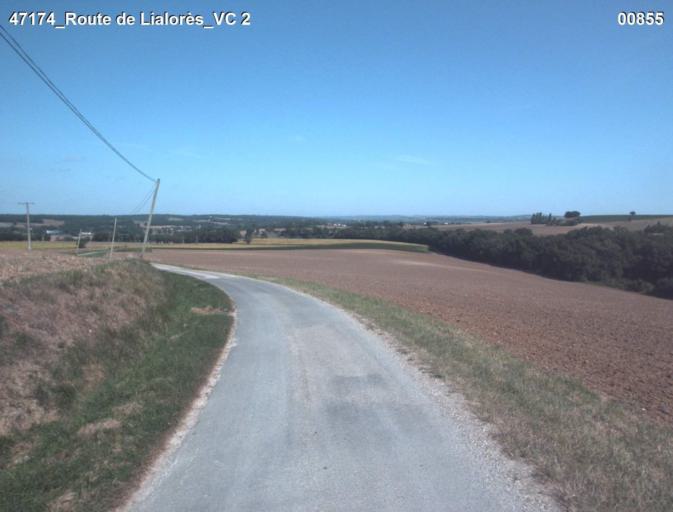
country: FR
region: Midi-Pyrenees
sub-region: Departement du Gers
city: Condom
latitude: 44.0145
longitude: 0.3780
